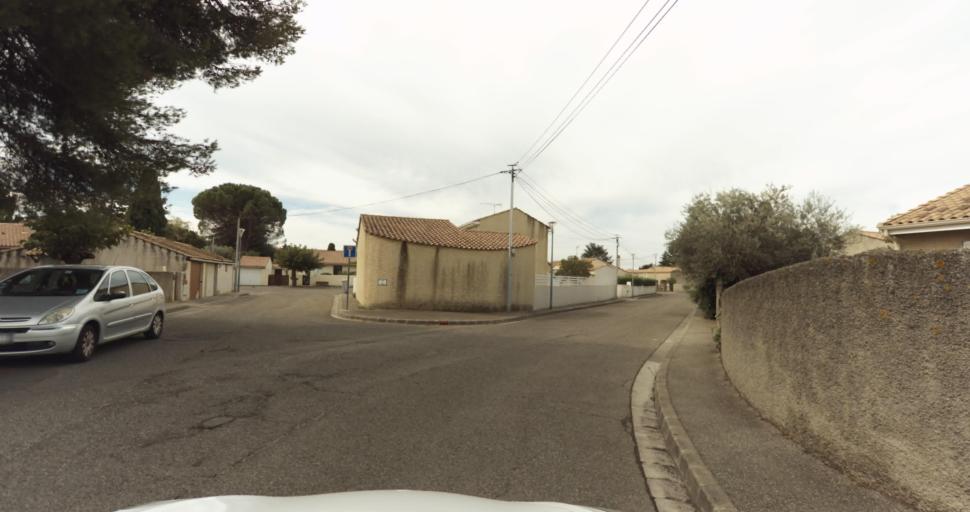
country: FR
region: Provence-Alpes-Cote d'Azur
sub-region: Departement des Bouches-du-Rhone
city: Miramas
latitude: 43.5930
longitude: 5.0035
